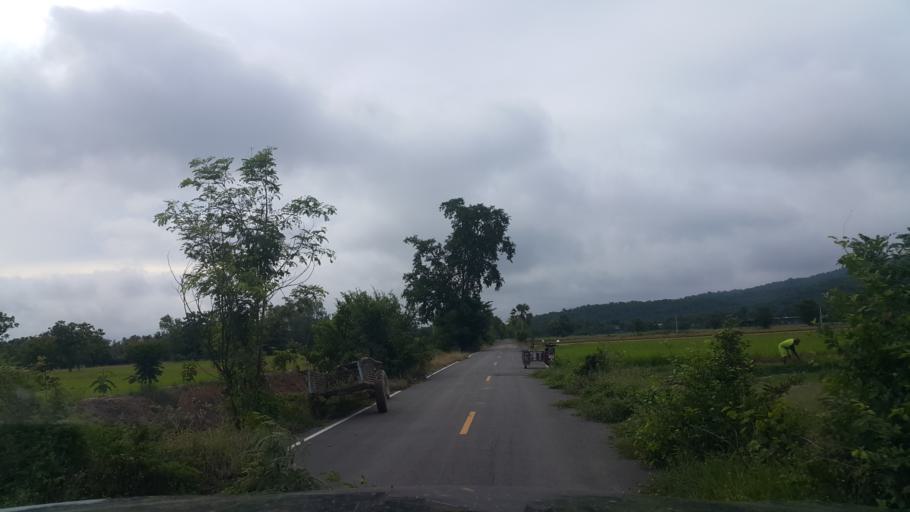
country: TH
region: Sukhothai
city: Sawankhalok
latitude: 17.3094
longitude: 99.7003
